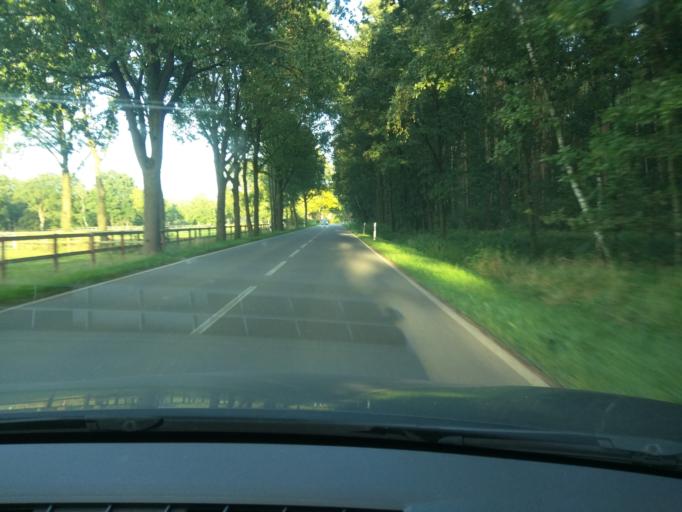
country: DE
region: Lower Saxony
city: Artlenburg
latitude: 53.3796
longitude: 10.4648
